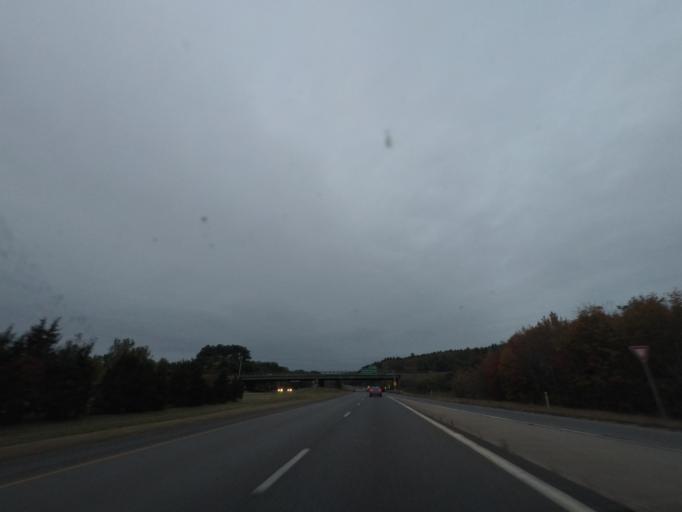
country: US
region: Massachusetts
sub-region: Worcester County
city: Oxford
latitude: 42.1150
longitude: -71.8546
